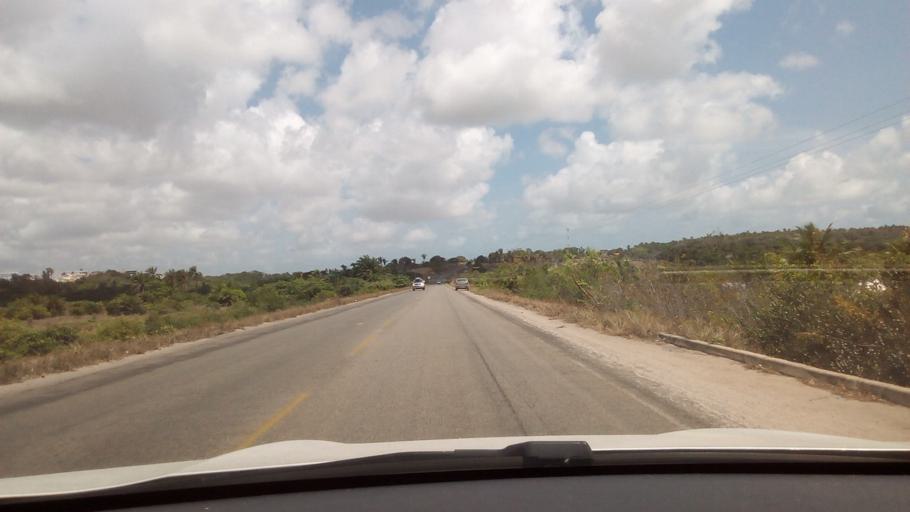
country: BR
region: Paraiba
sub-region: Conde
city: Conde
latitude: -7.2328
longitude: -34.8424
